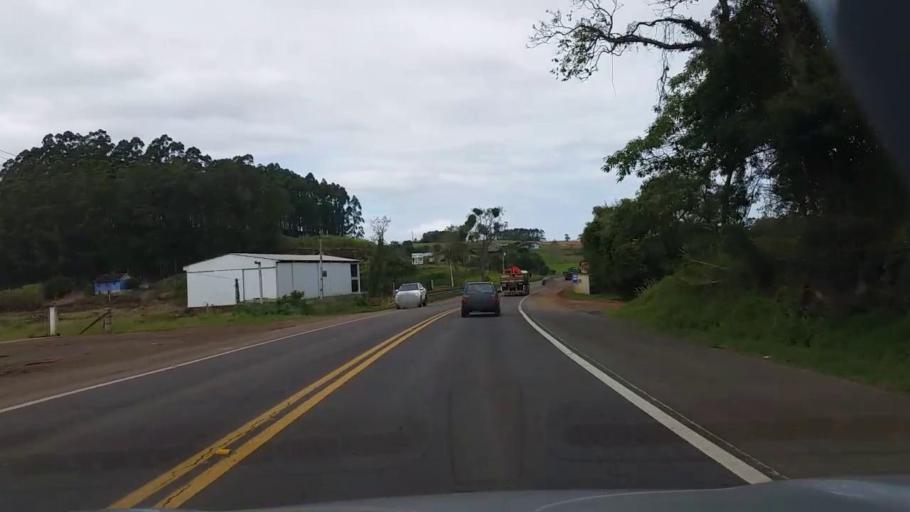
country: BR
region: Rio Grande do Sul
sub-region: Arroio Do Meio
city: Arroio do Meio
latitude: -29.4123
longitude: -52.0267
